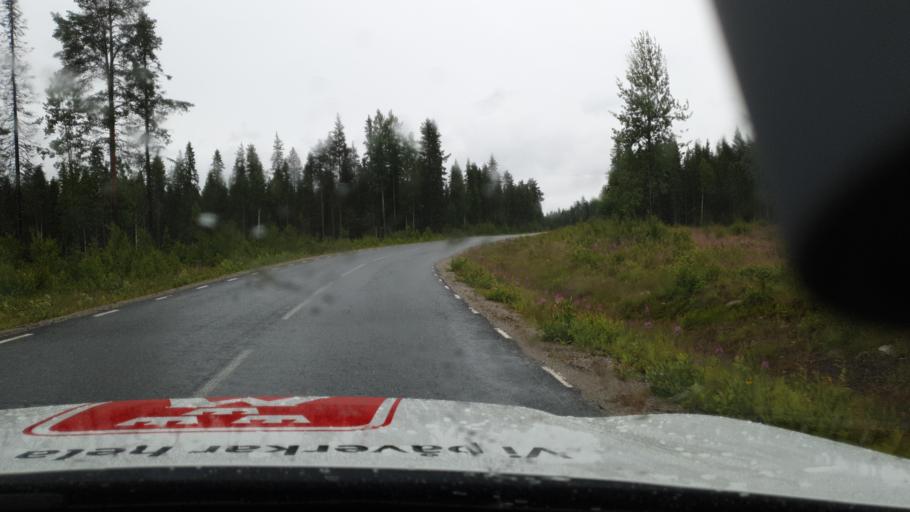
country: SE
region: Vaesterbotten
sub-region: Vindelns Kommun
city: Vindeln
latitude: 64.4736
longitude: 19.7623
